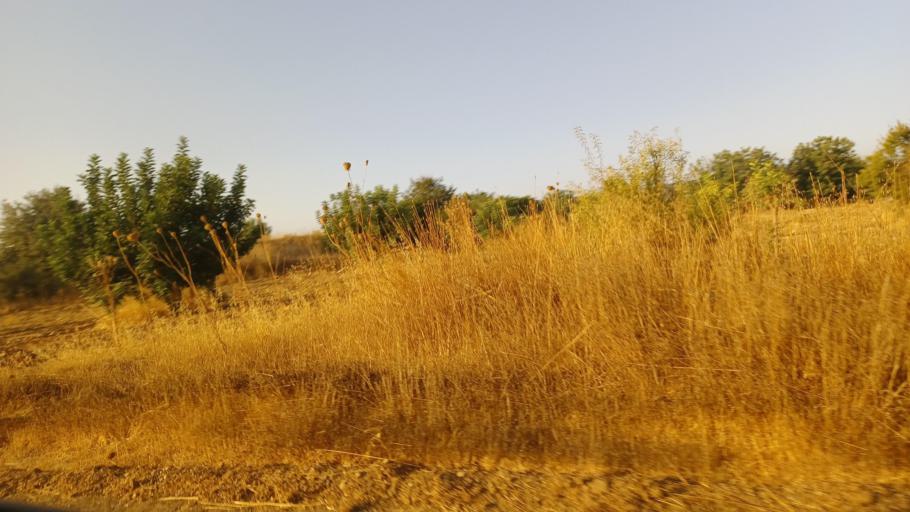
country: CY
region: Pafos
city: Polis
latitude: 34.9751
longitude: 32.4296
